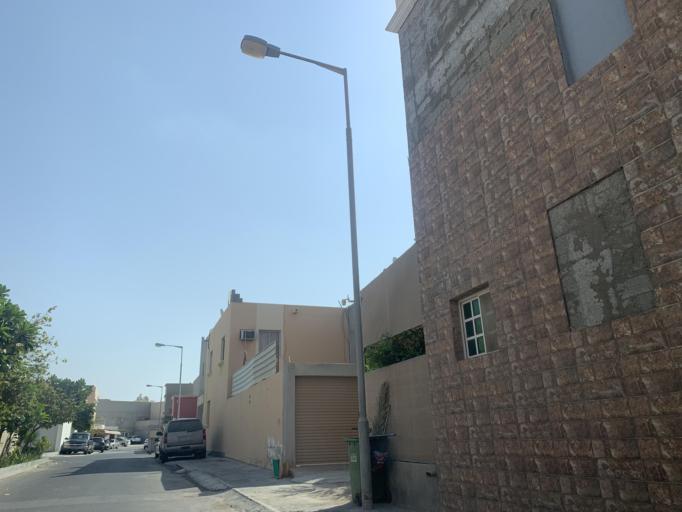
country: BH
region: Central Governorate
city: Madinat Hamad
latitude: 26.1374
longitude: 50.5070
